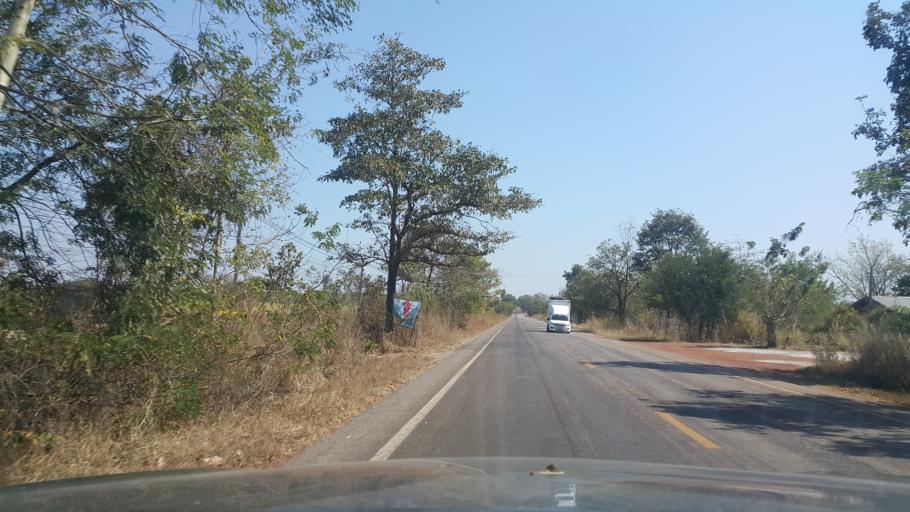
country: TH
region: Changwat Udon Thani
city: Ban Dung
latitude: 17.6089
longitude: 103.2873
